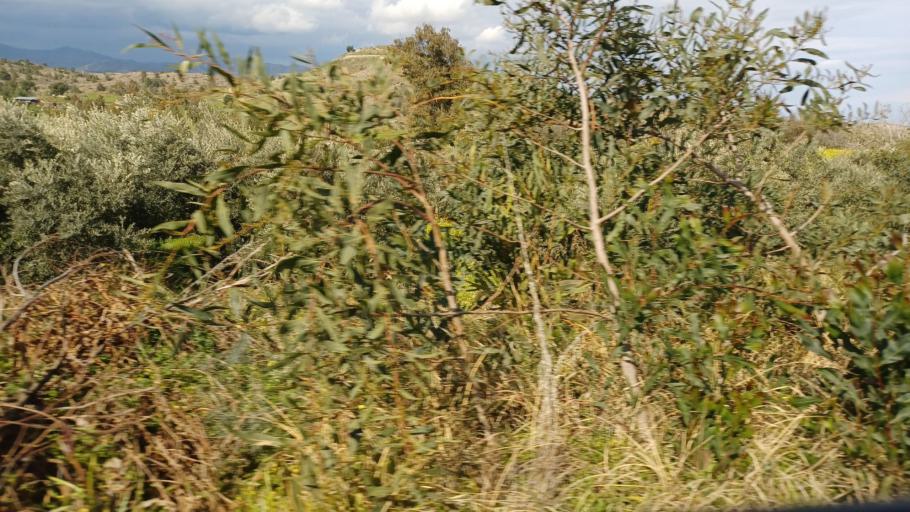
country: CY
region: Lefkosia
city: Lefka
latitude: 35.0986
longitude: 32.8860
